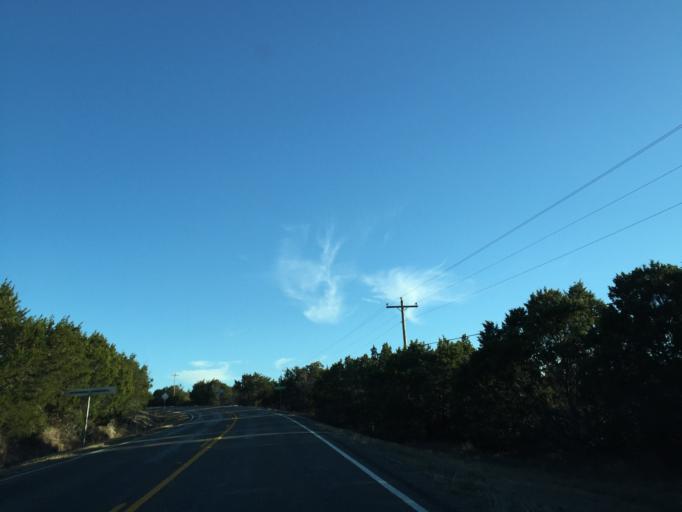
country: US
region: Texas
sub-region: Travis County
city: Lago Vista
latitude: 30.5129
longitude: -98.0411
